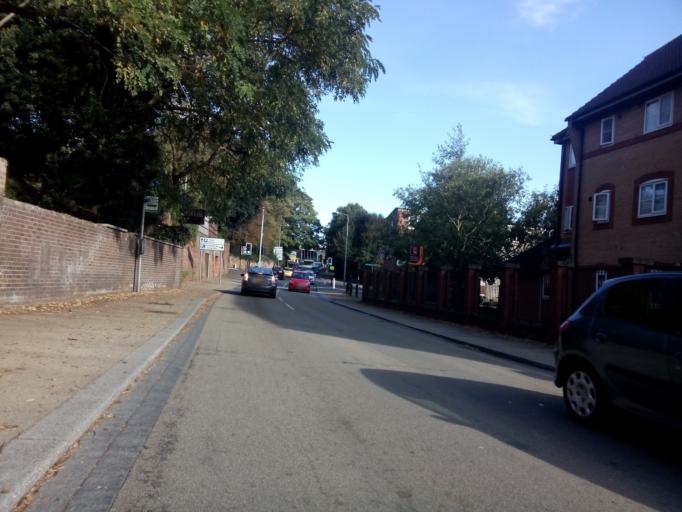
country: GB
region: England
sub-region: Suffolk
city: Ipswich
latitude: 52.0579
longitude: 1.1446
